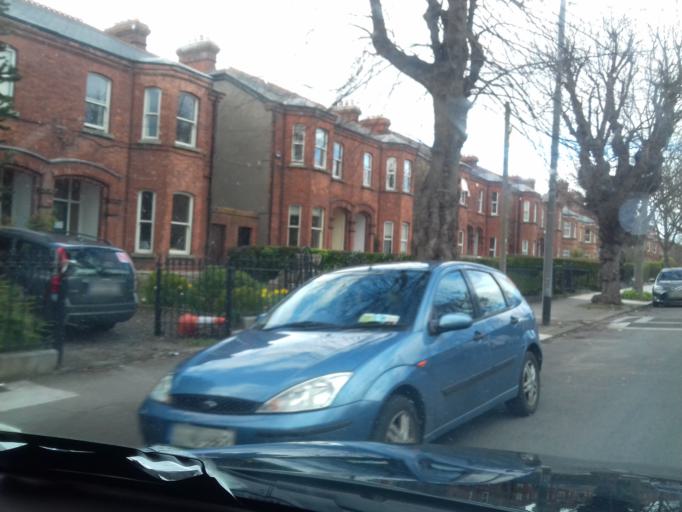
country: IE
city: Donnycarney
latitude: 53.3656
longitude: -6.2142
